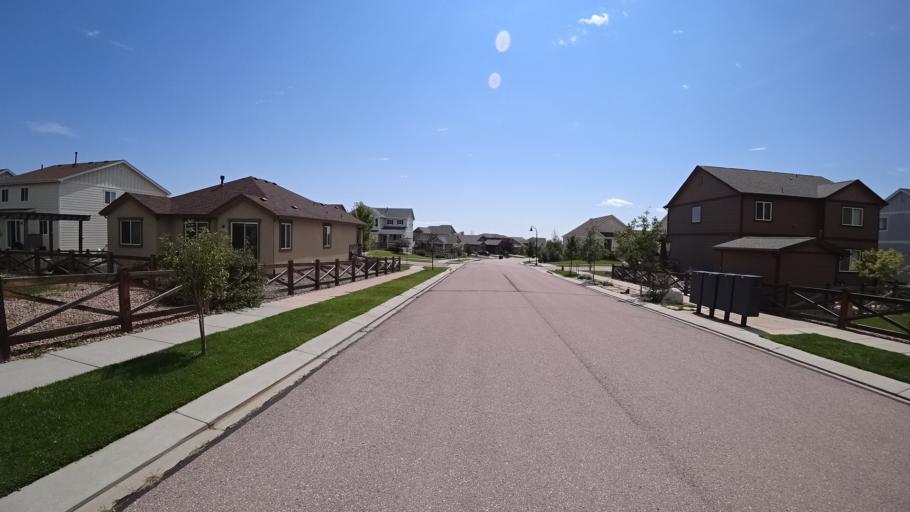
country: US
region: Colorado
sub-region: El Paso County
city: Cimarron Hills
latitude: 38.9304
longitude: -104.6766
